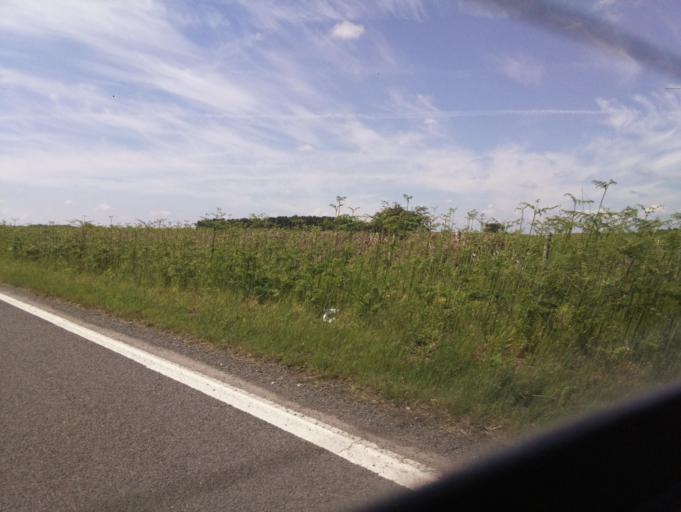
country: GB
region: England
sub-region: North Lincolnshire
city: Manton
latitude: 53.5246
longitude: -0.5795
